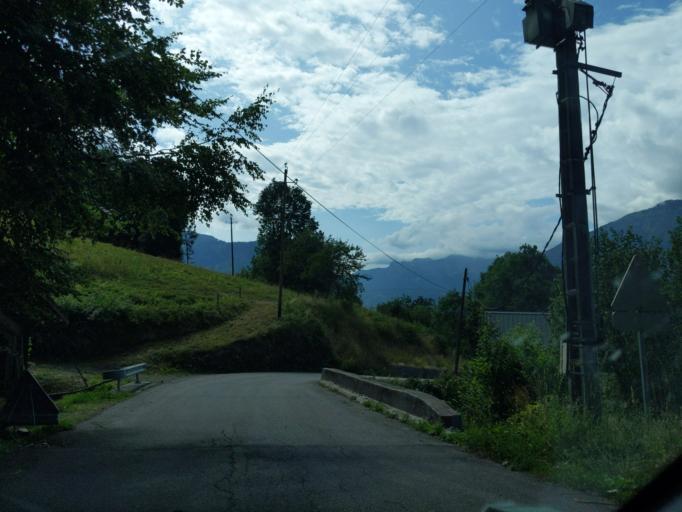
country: FR
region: Rhone-Alpes
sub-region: Departement de la Savoie
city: Ugine
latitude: 45.7481
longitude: 6.4537
